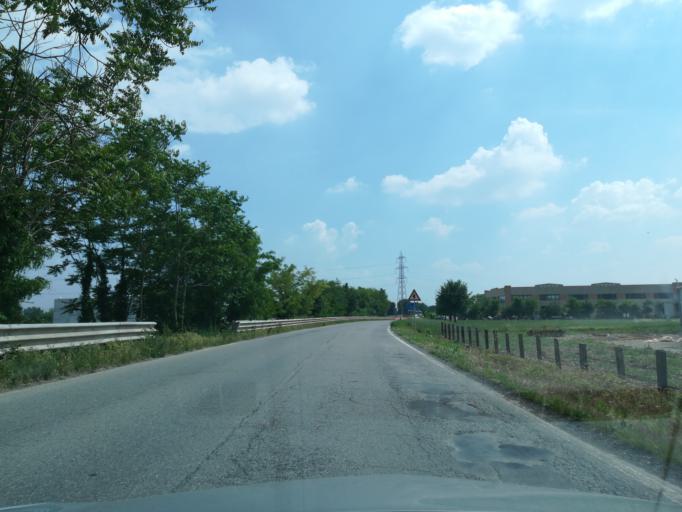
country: IT
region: Lombardy
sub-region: Provincia di Bergamo
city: Costa di Mezzate
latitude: 45.6513
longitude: 9.8082
